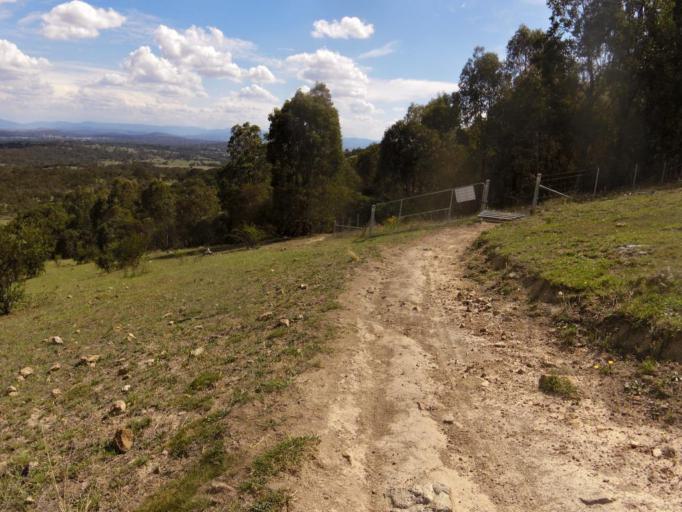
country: AU
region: Australian Capital Territory
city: Belconnen
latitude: -35.1476
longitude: 149.0914
